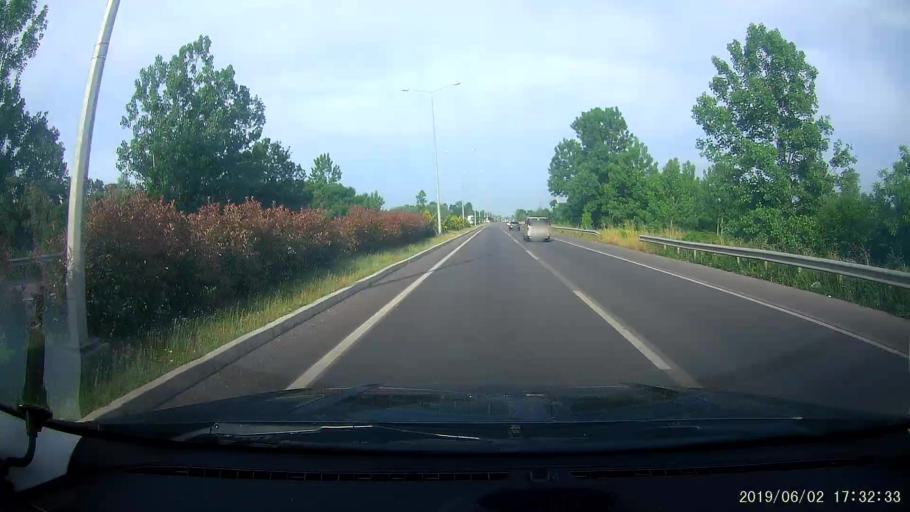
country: TR
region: Samsun
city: Carsamba
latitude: 41.2202
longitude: 36.8289
